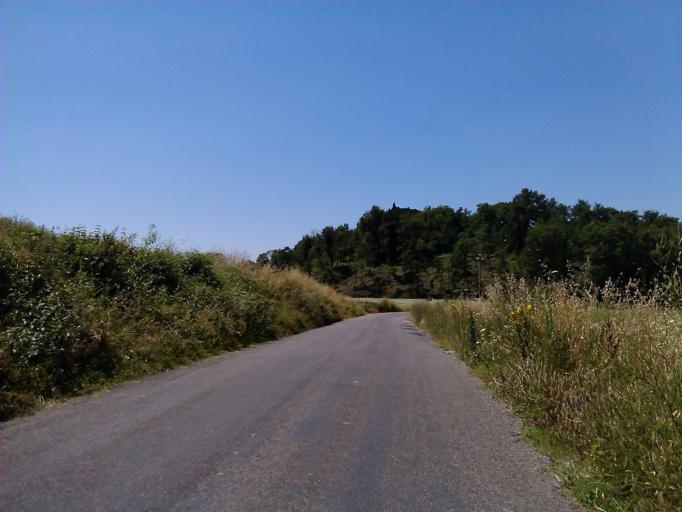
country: IT
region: Umbria
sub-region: Provincia di Terni
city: Fabro Scalo
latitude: 42.8602
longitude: 12.0463
